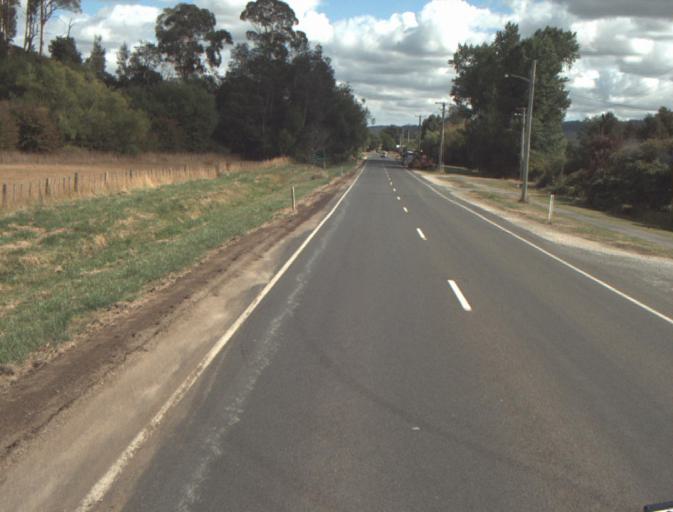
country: AU
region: Tasmania
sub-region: Launceston
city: Mayfield
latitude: -41.2578
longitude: 147.2175
